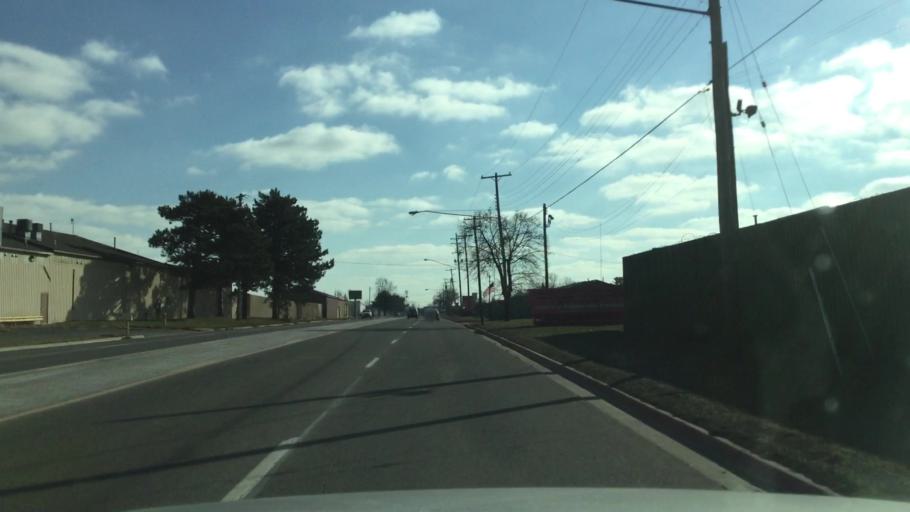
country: US
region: Michigan
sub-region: Genesee County
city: Flint
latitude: 43.0488
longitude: -83.6616
